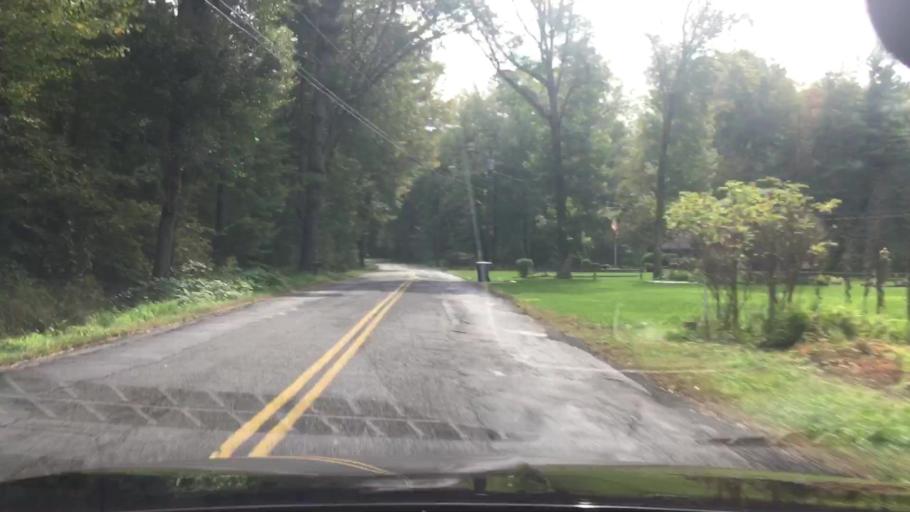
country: US
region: Connecticut
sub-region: Hartford County
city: Hazardville
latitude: 42.0038
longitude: -72.5084
